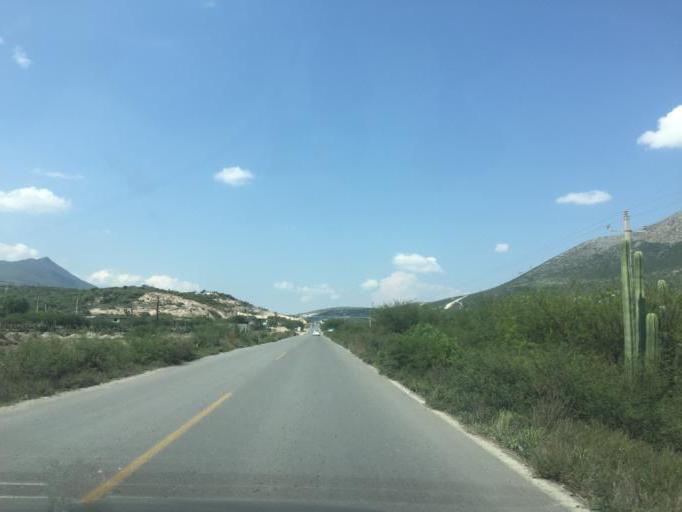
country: MX
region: Hidalgo
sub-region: Cardonal
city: Pozuelos
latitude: 20.5871
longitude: -99.1271
